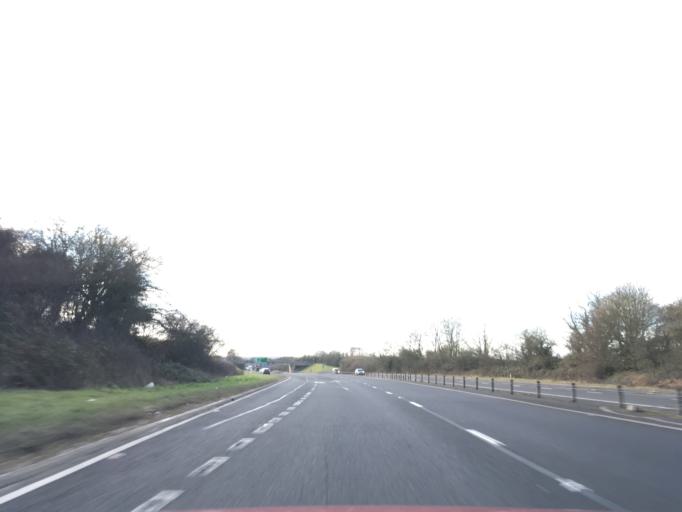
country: GB
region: Wales
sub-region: Monmouthshire
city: Llanarth
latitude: 51.7703
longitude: -2.8301
